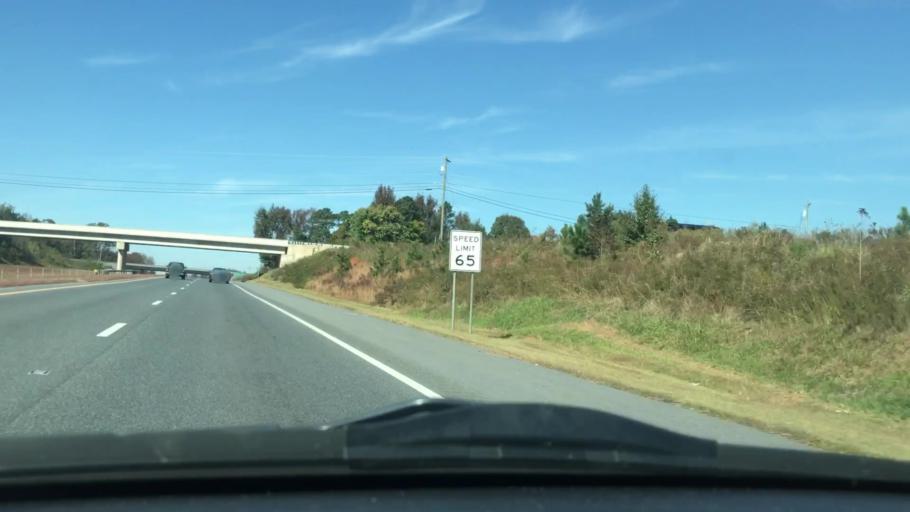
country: US
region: North Carolina
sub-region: Randolph County
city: Randleman
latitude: 35.8312
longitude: -79.8585
